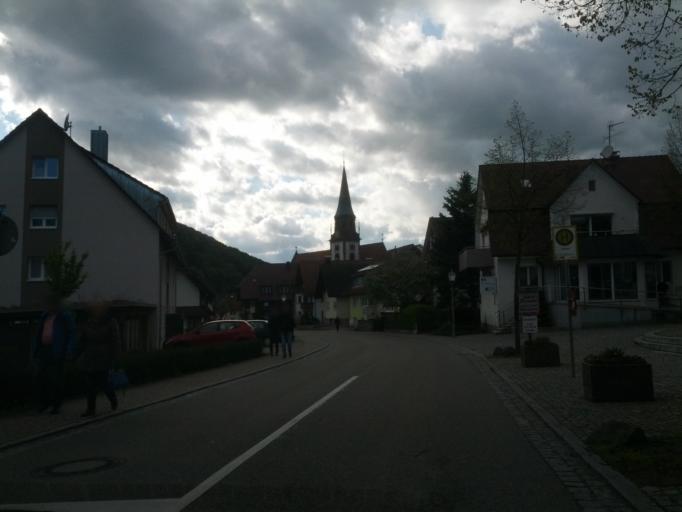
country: DE
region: Baden-Wuerttemberg
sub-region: Freiburg Region
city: Glottertal
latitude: 48.0492
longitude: 7.9428
